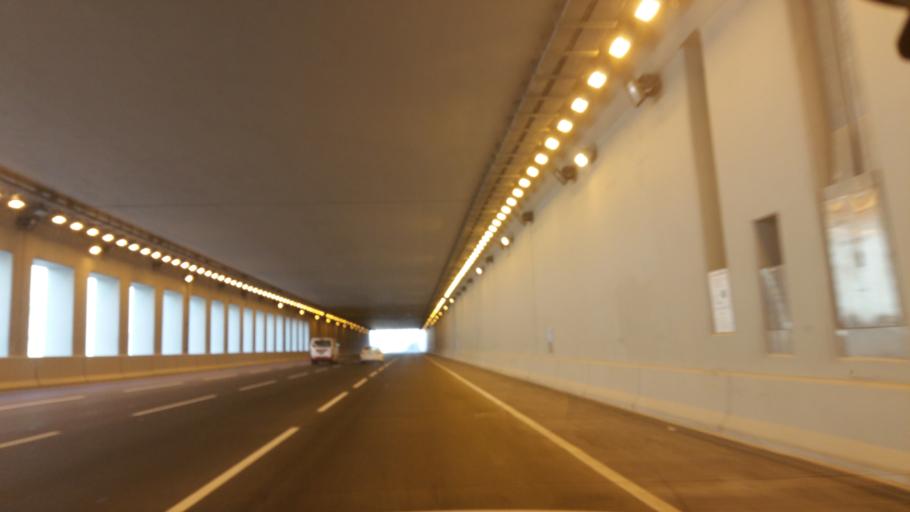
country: QA
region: Baladiyat ar Rayyan
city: Ar Rayyan
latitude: 25.2972
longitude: 51.4448
